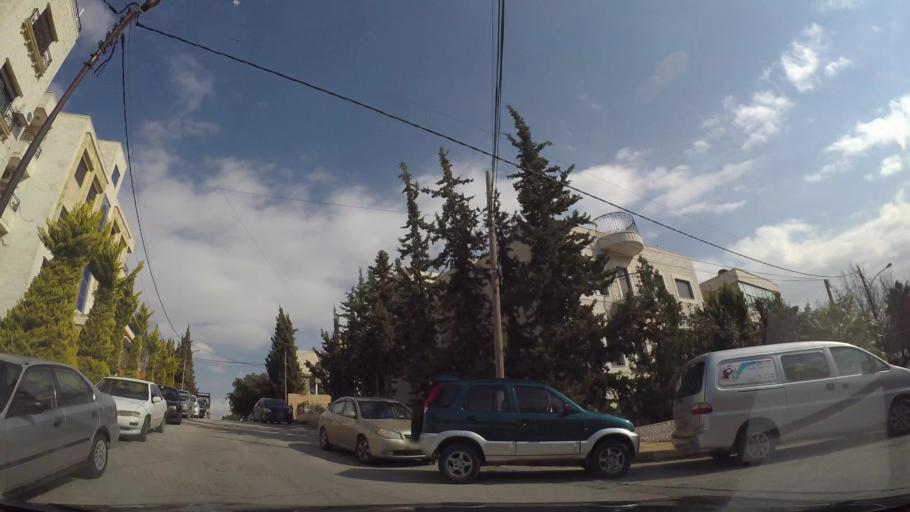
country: JO
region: Amman
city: Al Jubayhah
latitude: 31.9726
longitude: 35.8881
